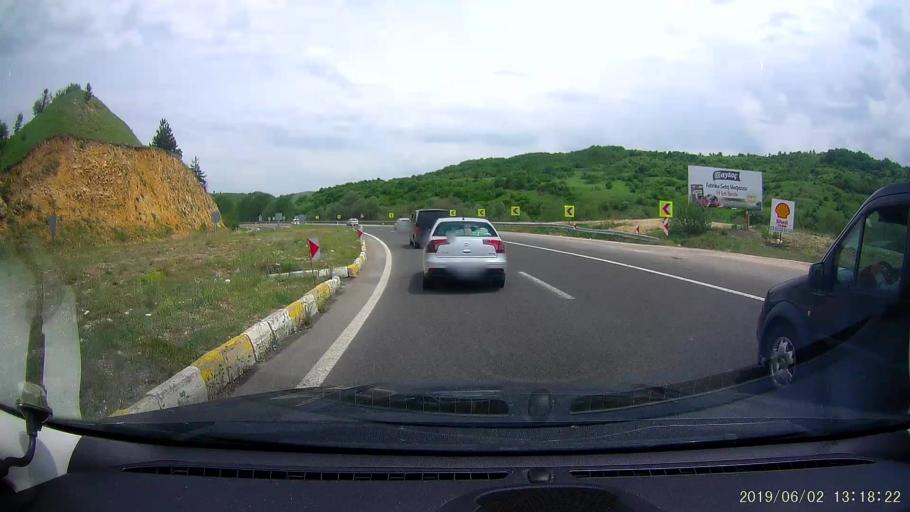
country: TR
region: Karabuk
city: Gozyeri
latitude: 40.8350
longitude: 32.7169
